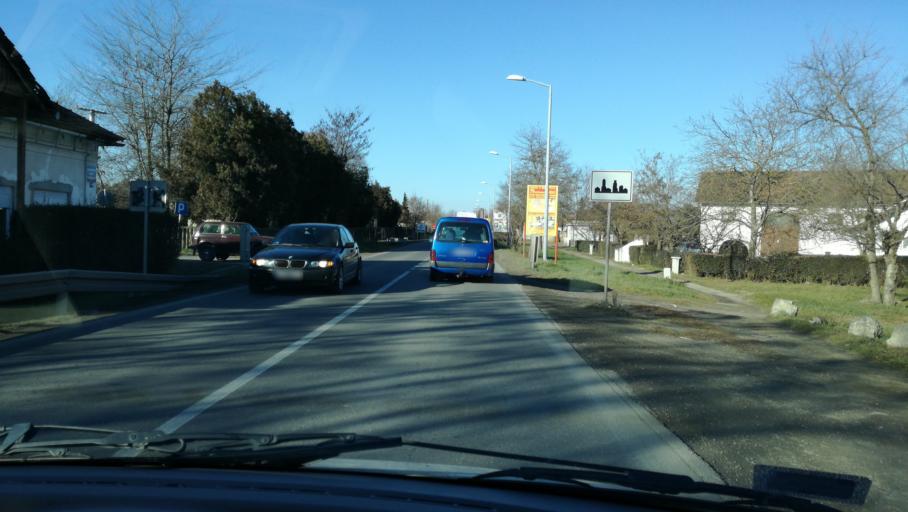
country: RS
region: Autonomna Pokrajina Vojvodina
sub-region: Severnobacki Okrug
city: Subotica
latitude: 46.0854
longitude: 19.6881
